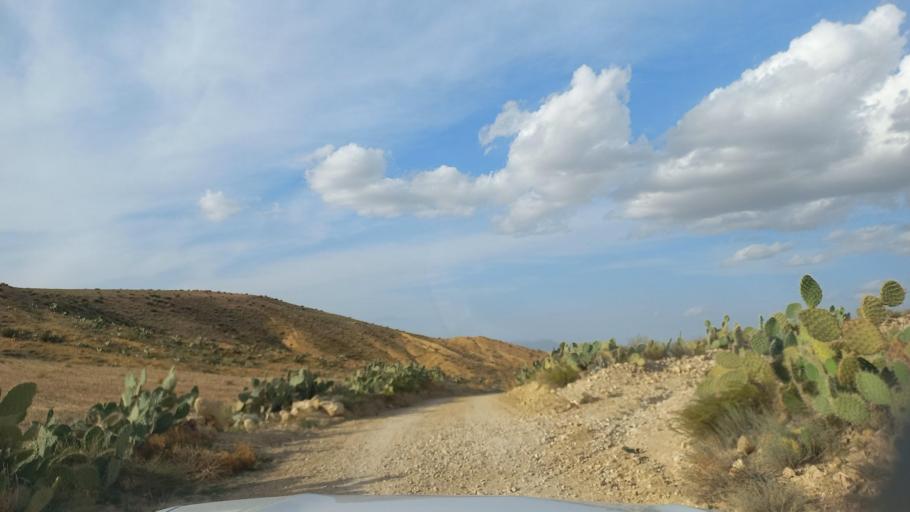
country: TN
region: Al Qasrayn
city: Sbiba
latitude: 35.4586
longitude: 9.0825
